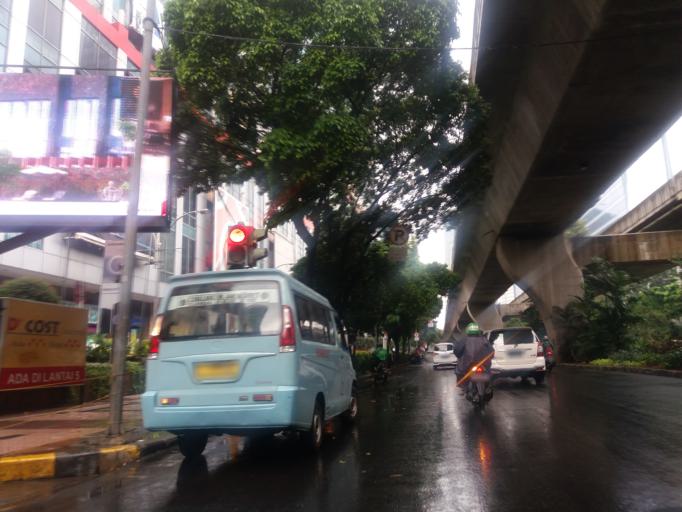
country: ID
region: Jakarta Raya
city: Jakarta
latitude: -6.2243
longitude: 106.8269
